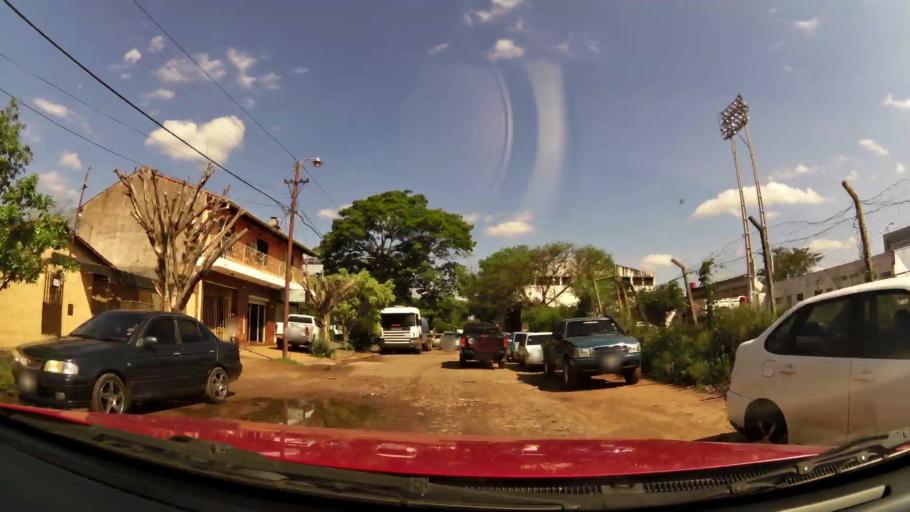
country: PY
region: Central
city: San Lorenzo
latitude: -25.3424
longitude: -57.5001
